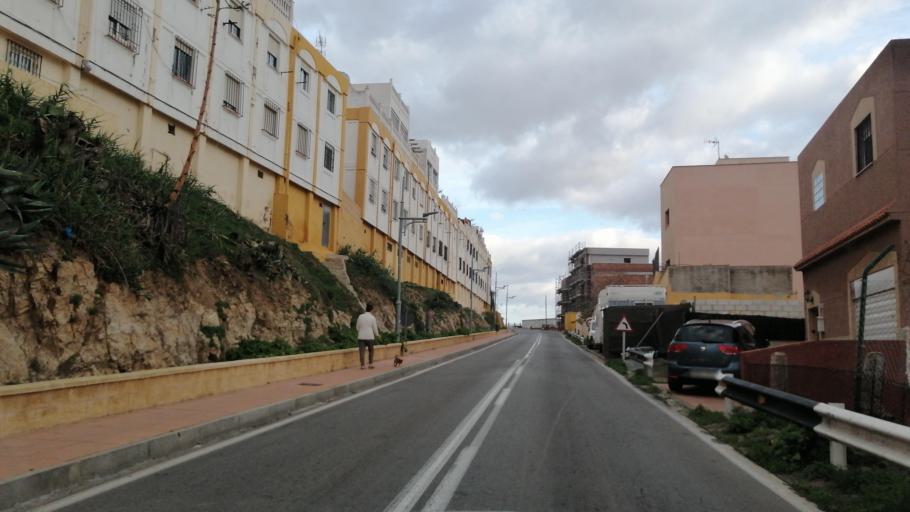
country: ES
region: Ceuta
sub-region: Ceuta
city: Ceuta
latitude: 35.8902
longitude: -5.2947
